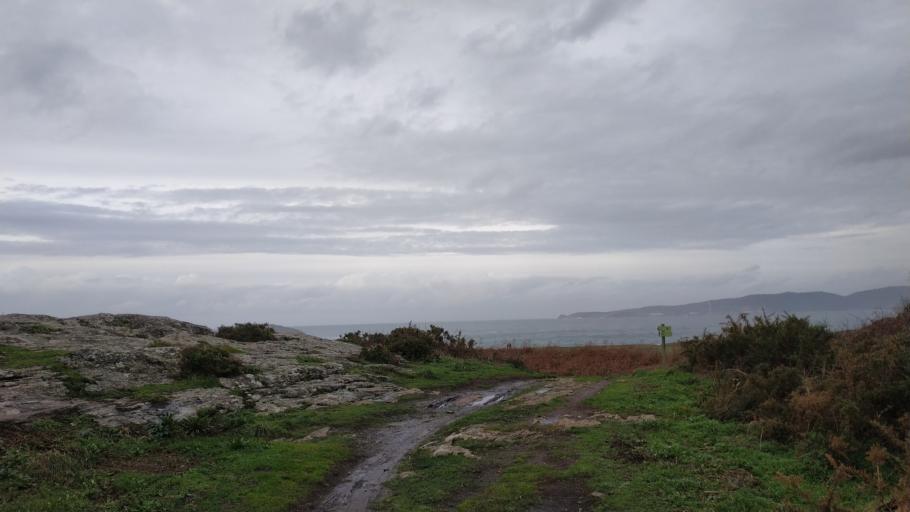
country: ES
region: Galicia
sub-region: Provincia da Coruna
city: Oleiros
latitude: 43.4004
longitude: -8.3298
